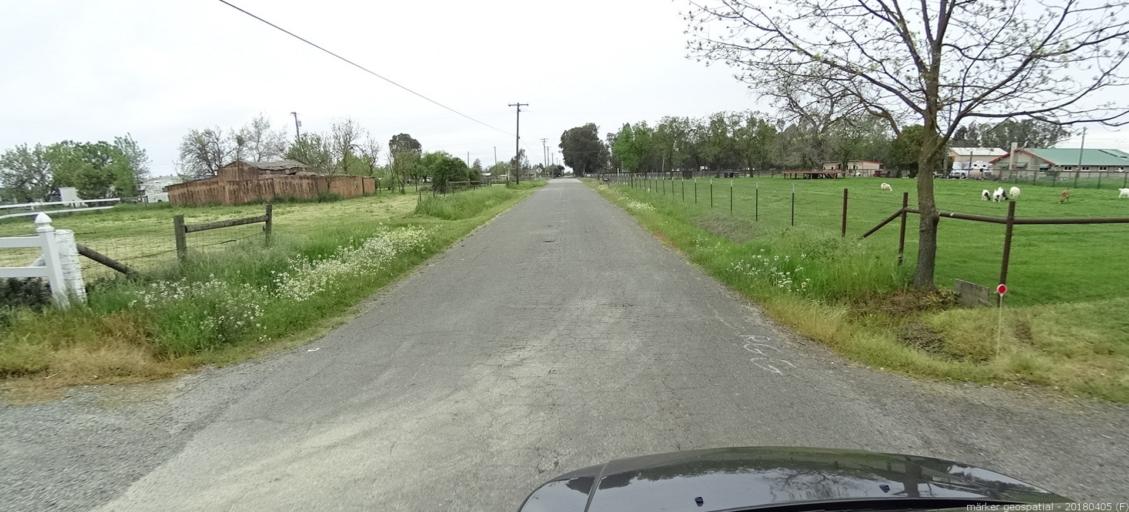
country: US
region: California
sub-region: Sacramento County
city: Herald
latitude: 38.2811
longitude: -121.2365
